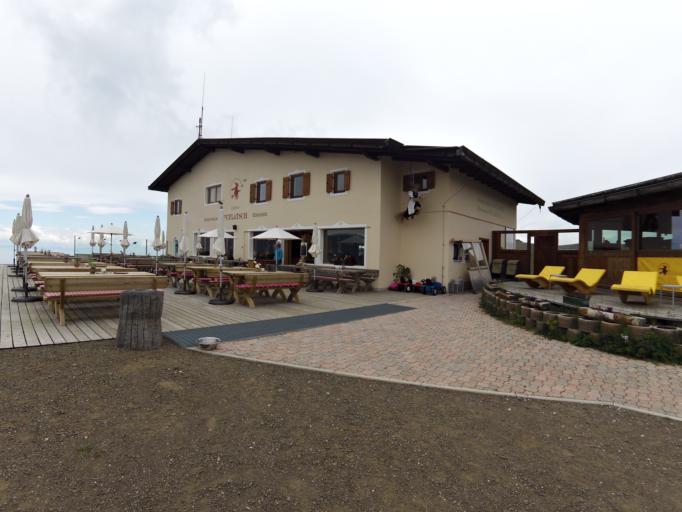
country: IT
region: Trentino-Alto Adige
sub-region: Bolzano
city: Ortisei
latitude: 46.5515
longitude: 11.6165
